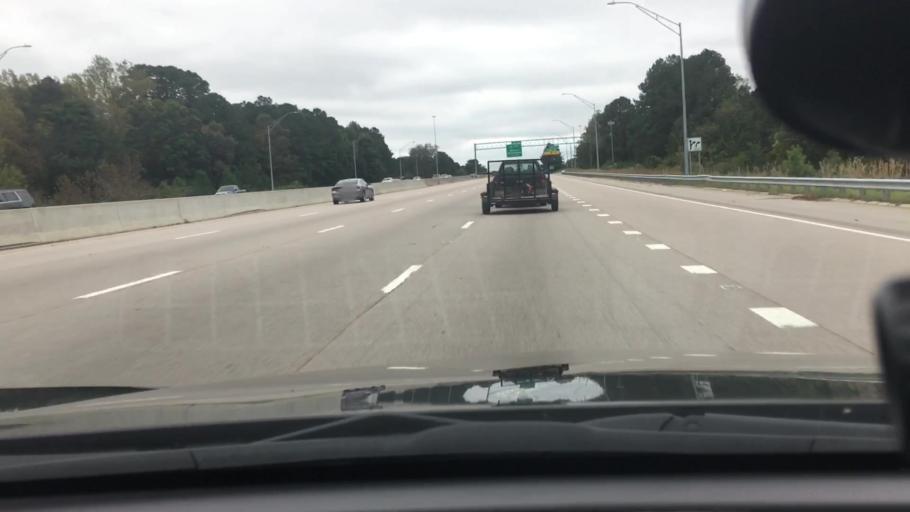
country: US
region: North Carolina
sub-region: Wake County
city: Raleigh
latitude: 35.7741
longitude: -78.5740
